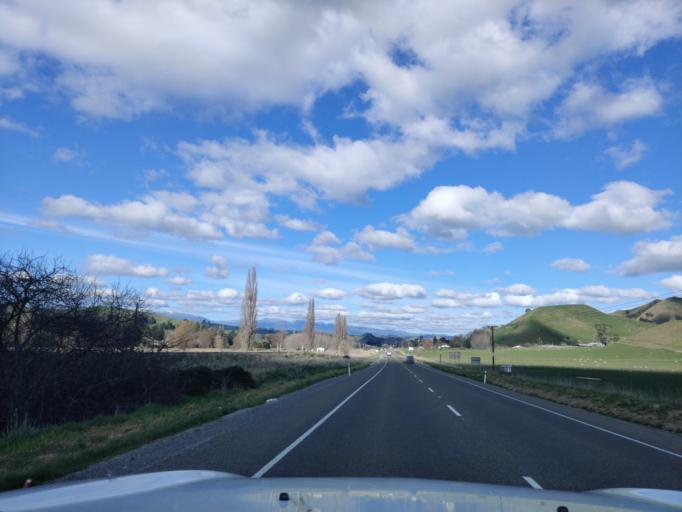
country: NZ
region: Manawatu-Wanganui
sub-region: Ruapehu District
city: Waiouru
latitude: -39.6992
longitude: 175.8267
